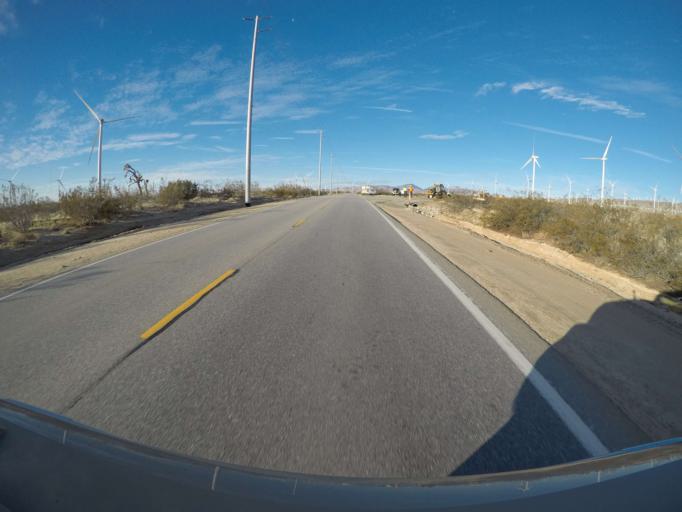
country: US
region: California
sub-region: Kern County
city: Mojave
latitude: 35.0425
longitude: -118.2312
